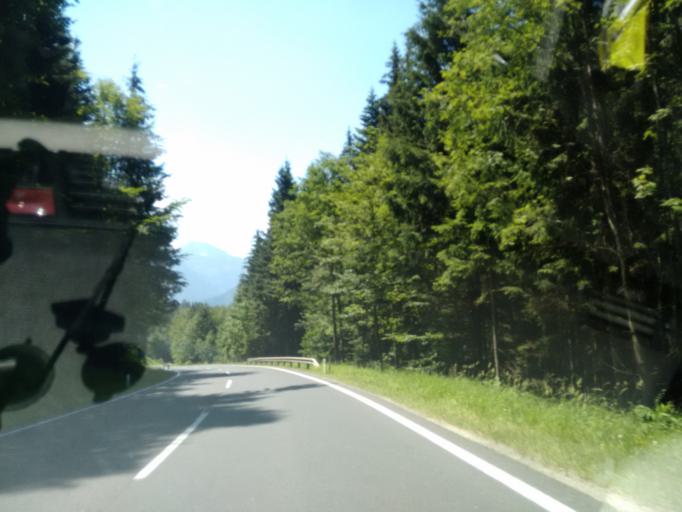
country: AT
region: Upper Austria
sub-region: Politischer Bezirk Gmunden
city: Bad Goisern
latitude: 47.6231
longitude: 13.6812
